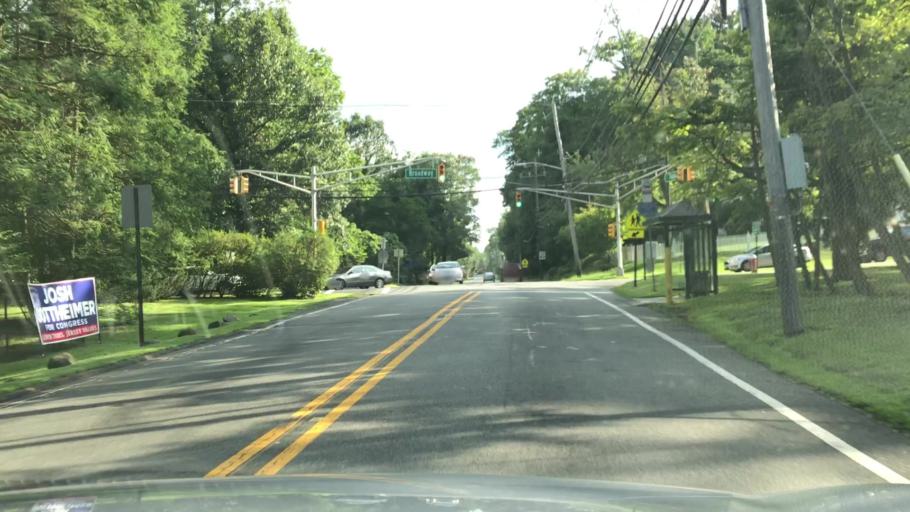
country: US
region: New Jersey
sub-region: Bergen County
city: Norwood
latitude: 40.9989
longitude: -73.9619
